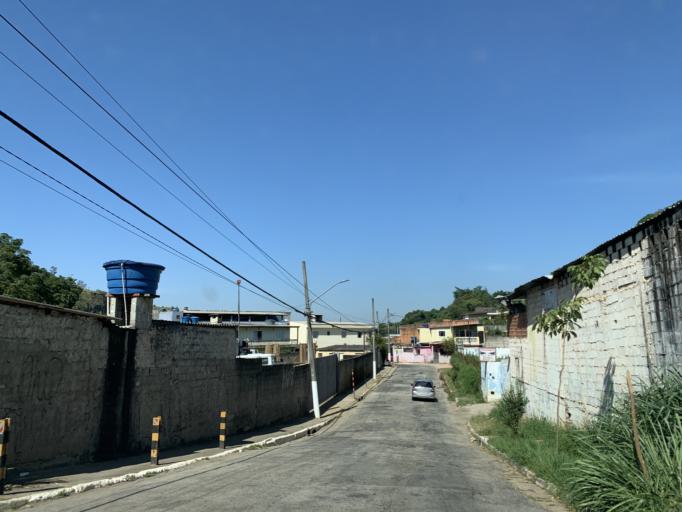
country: BR
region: Sao Paulo
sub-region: Osasco
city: Osasco
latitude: -23.4604
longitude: -46.7426
